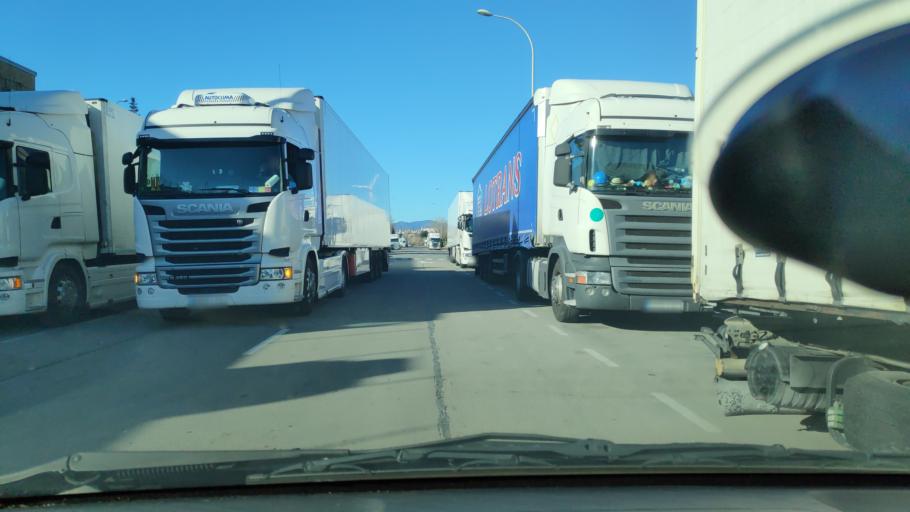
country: ES
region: Catalonia
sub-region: Provincia de Barcelona
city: Sant Quirze del Valles
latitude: 41.5211
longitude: 2.0935
